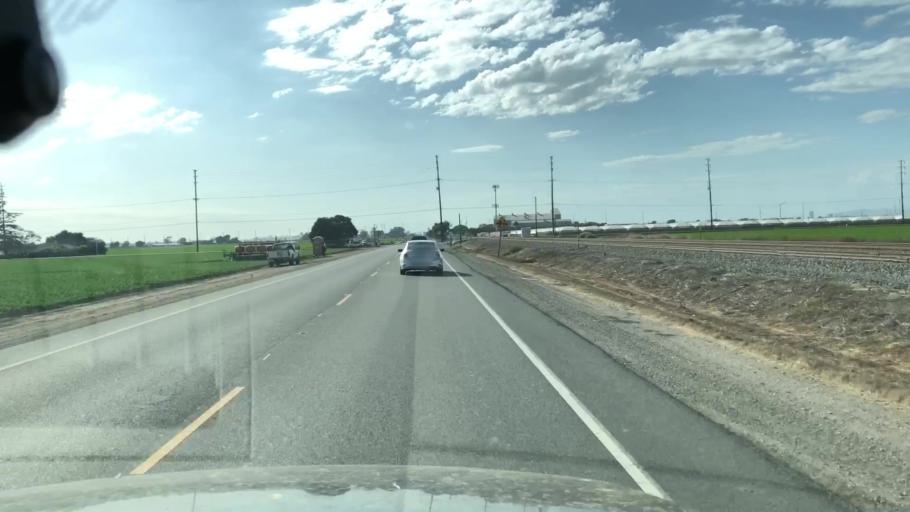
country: US
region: California
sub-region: Ventura County
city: Camarillo
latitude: 34.1966
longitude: -119.0934
